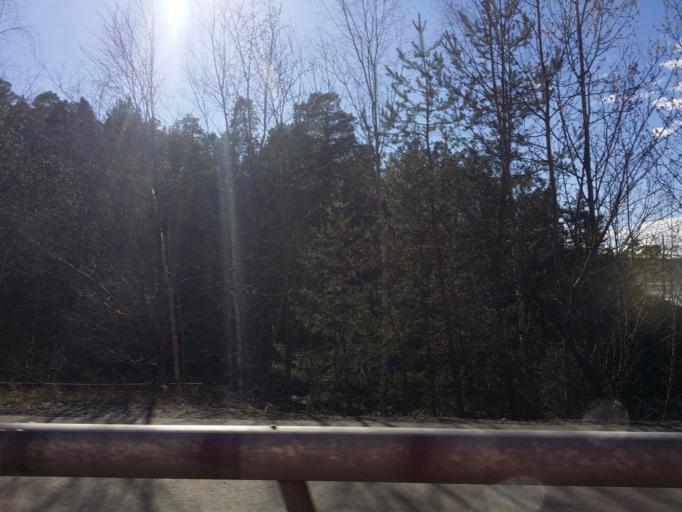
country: NO
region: Akershus
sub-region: Oppegard
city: Kolbotn
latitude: 59.8422
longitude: 10.7759
